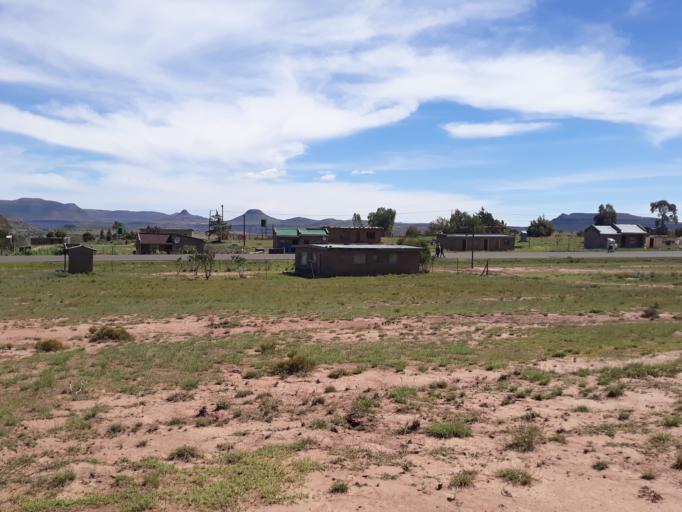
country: LS
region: Quthing
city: Quthing
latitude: -30.3352
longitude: 27.5353
